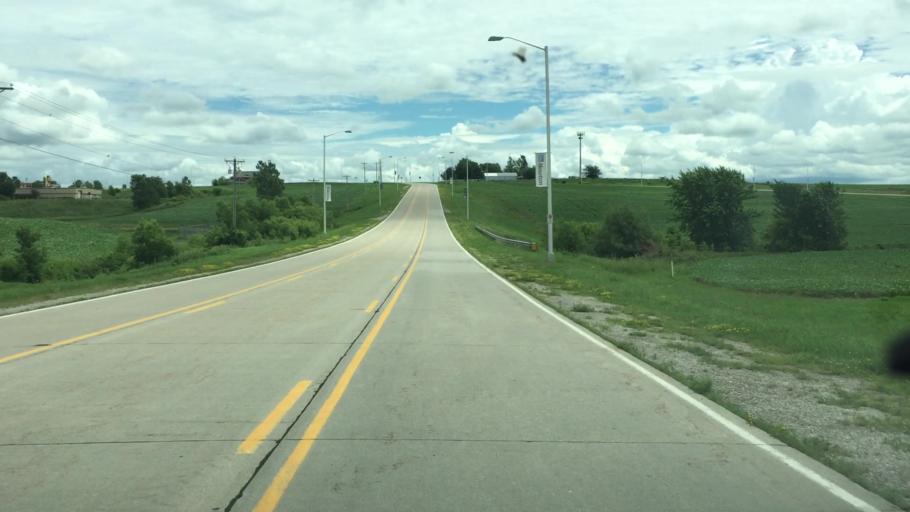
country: US
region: Iowa
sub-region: Jasper County
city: Newton
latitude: 41.6777
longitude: -93.0065
